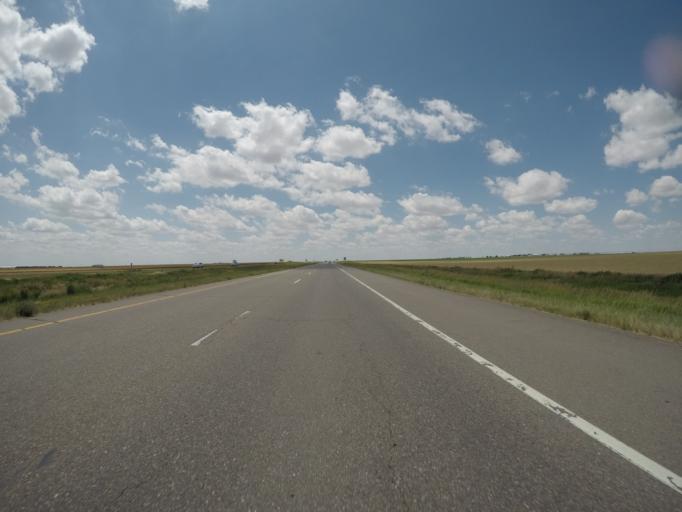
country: US
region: Colorado
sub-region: Kit Carson County
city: Burlington
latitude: 39.2943
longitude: -102.2871
